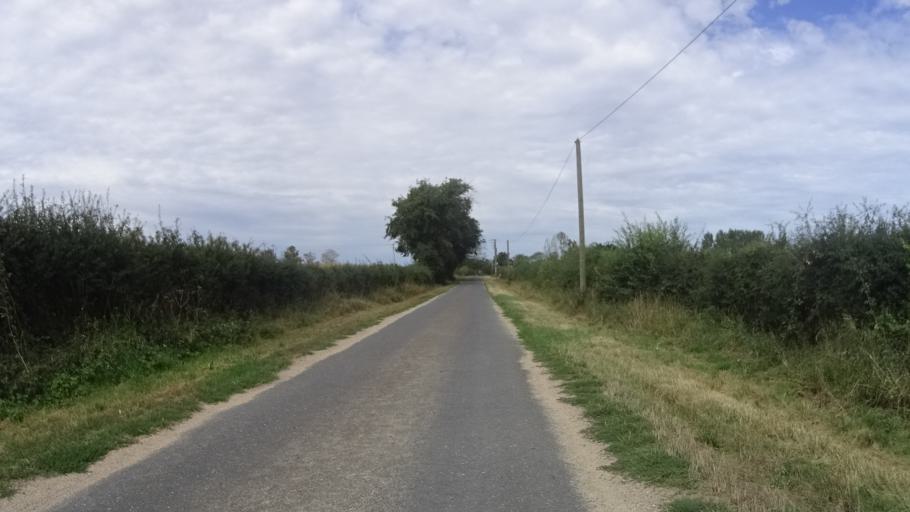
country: FR
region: Auvergne
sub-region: Departement de l'Allier
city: Beaulon
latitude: 46.6540
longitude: 3.6648
